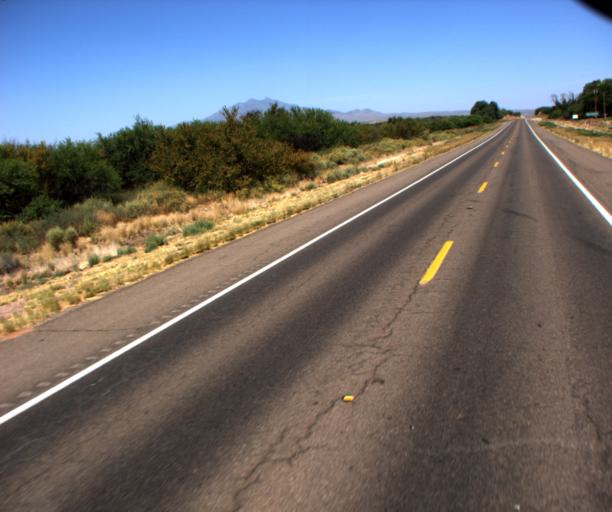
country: US
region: Arizona
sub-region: Graham County
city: Bylas
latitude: 33.0757
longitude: -110.0304
